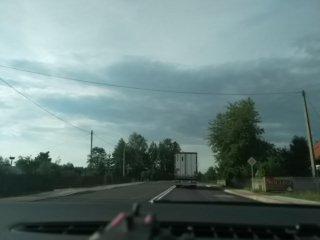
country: PL
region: Subcarpathian Voivodeship
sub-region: Powiat nizanski
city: Jarocin
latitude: 50.6441
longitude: 22.2856
